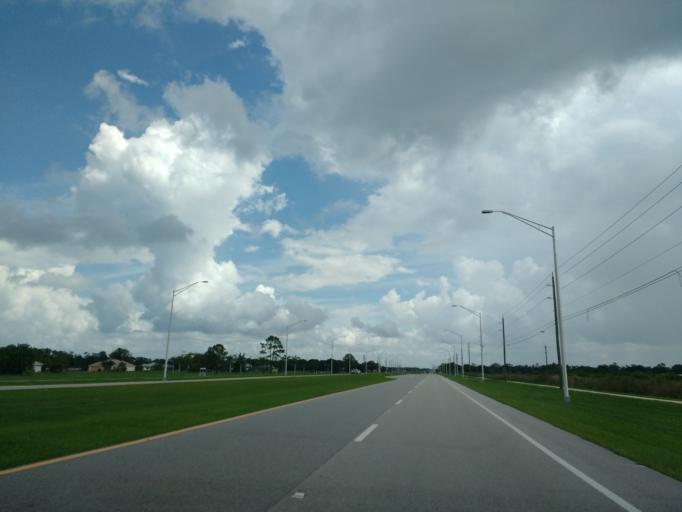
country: US
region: Florida
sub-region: Lee County
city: Burnt Store Marina
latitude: 26.7782
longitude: -82.0379
